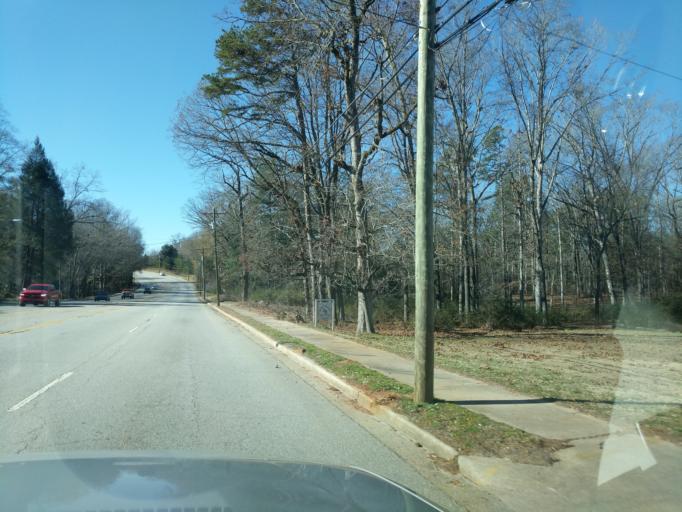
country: US
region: South Carolina
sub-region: Oconee County
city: Westminster
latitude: 34.6624
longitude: -83.0762
